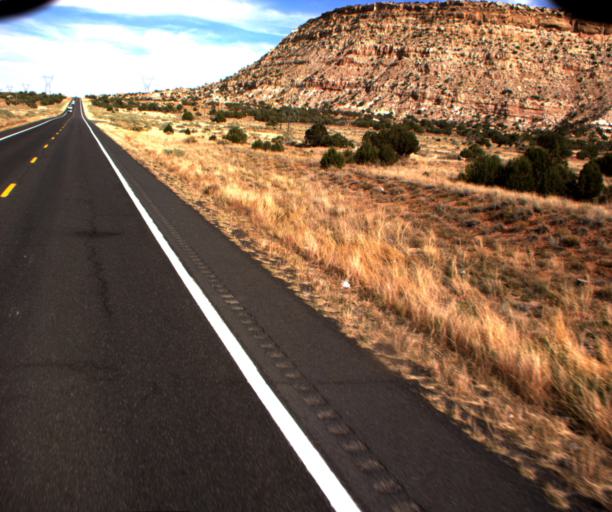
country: US
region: Arizona
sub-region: Navajo County
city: Kayenta
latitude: 36.6876
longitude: -110.3741
